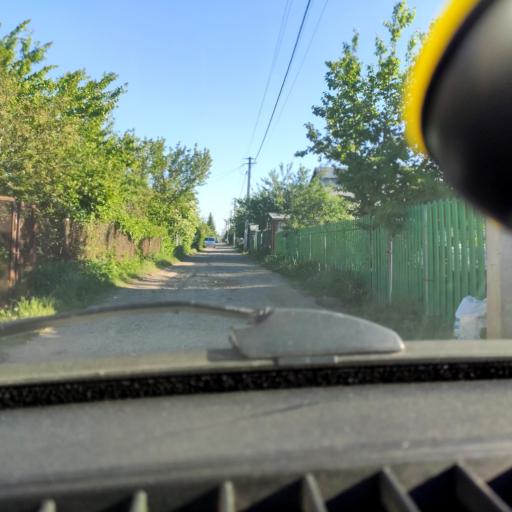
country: RU
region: Samara
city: Tol'yatti
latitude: 53.5963
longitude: 49.3160
